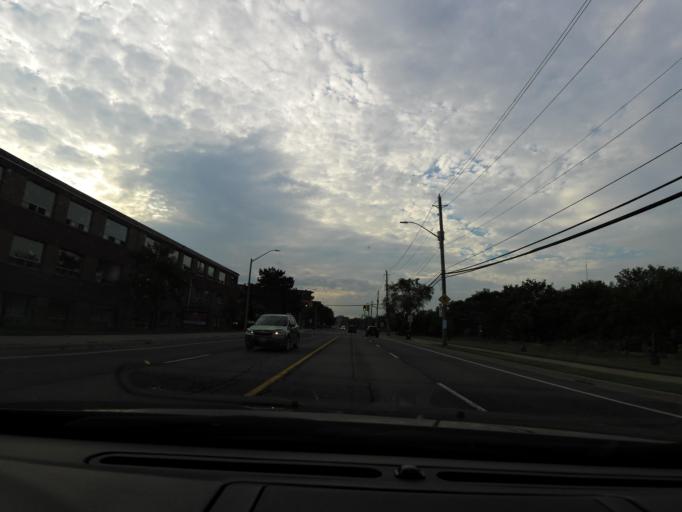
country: CA
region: Ontario
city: Hamilton
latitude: 43.2241
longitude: -79.7849
